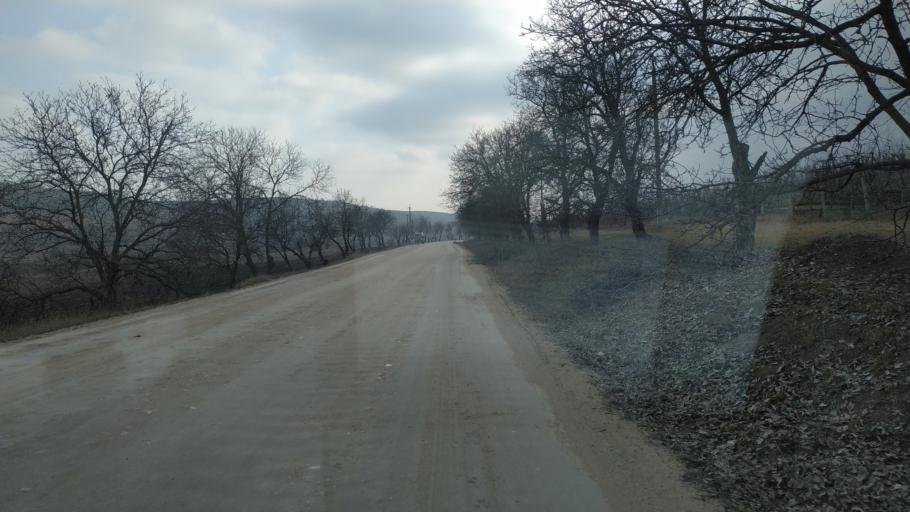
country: MD
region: Hincesti
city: Dancu
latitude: 46.9186
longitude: 28.3289
